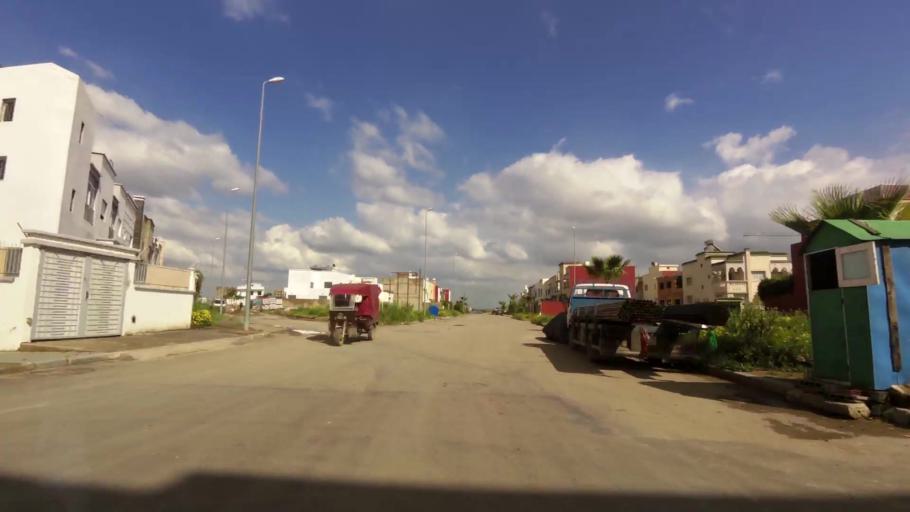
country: MA
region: Chaouia-Ouardigha
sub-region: Settat Province
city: Berrechid
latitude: 33.2581
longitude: -7.5666
